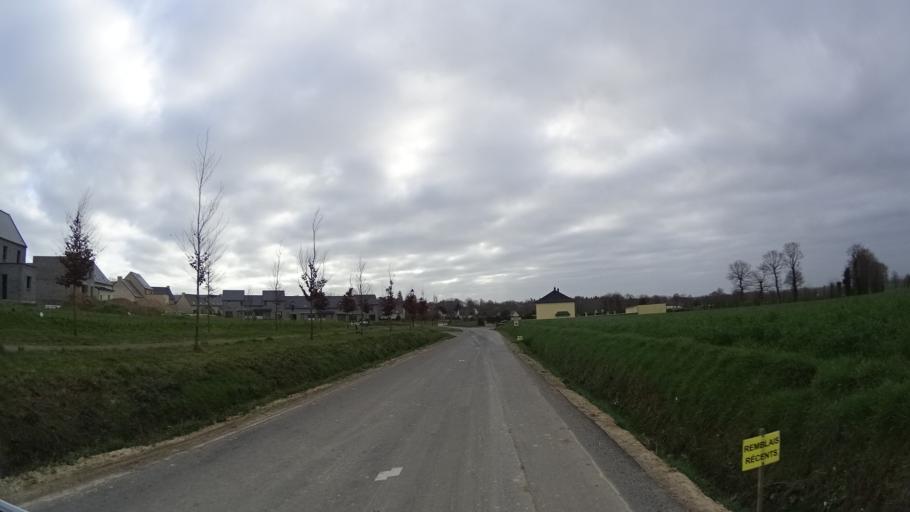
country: FR
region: Brittany
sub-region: Departement d'Ille-et-Vilaine
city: Saint-Gilles
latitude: 48.1778
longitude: -1.8610
